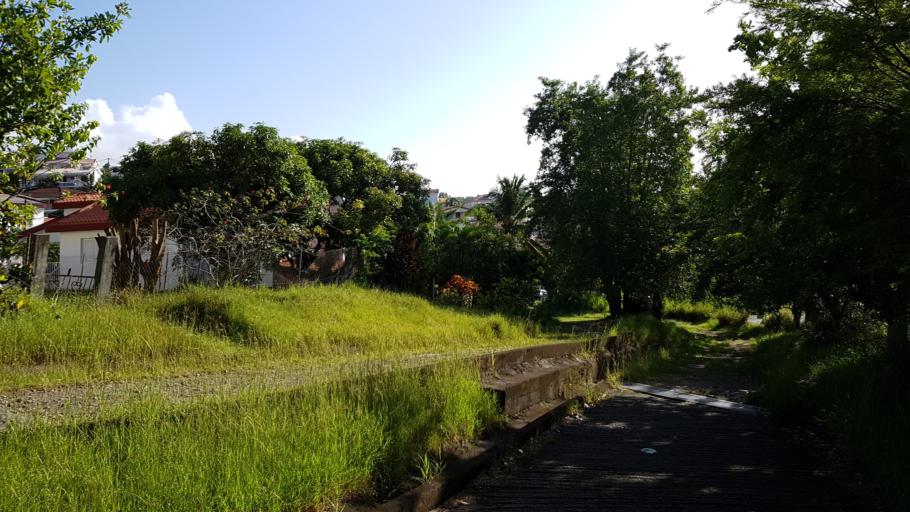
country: MQ
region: Martinique
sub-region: Martinique
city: Fort-de-France
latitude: 14.6298
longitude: -61.0987
